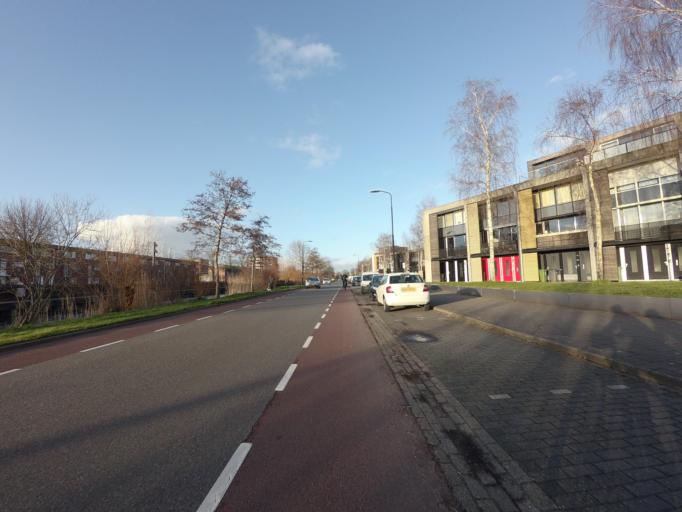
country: NL
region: Utrecht
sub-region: Gemeente IJsselstein
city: IJsselstein
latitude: 52.0118
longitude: 5.0436
